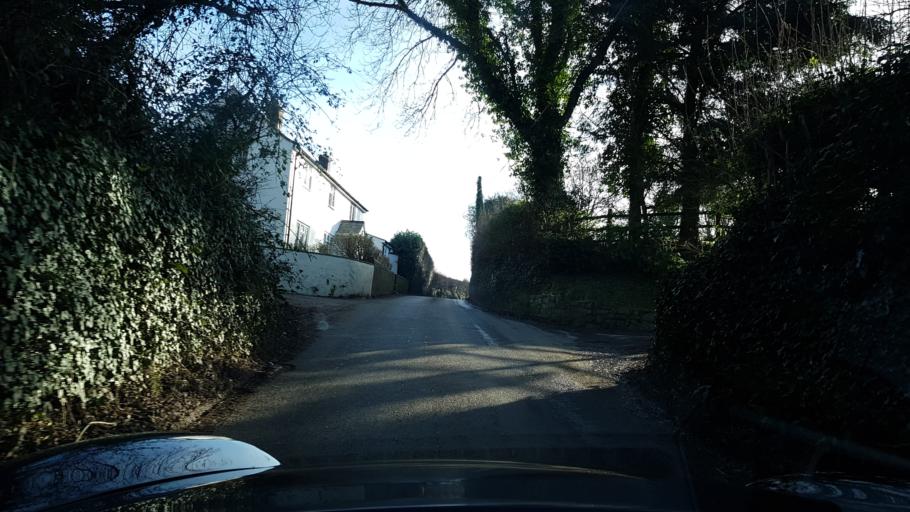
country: GB
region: England
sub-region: Dorset
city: Bridport
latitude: 50.7569
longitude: -2.7753
